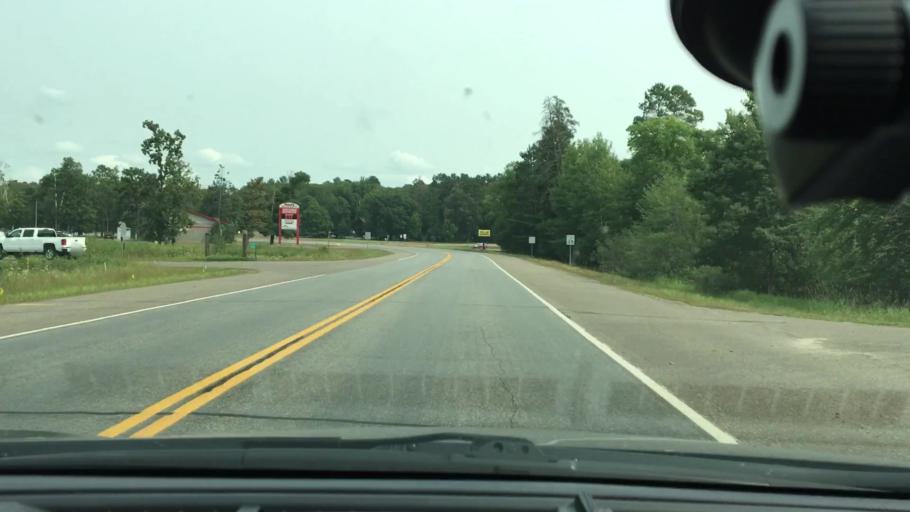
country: US
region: Minnesota
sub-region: Crow Wing County
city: Cross Lake
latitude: 46.6686
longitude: -94.1071
